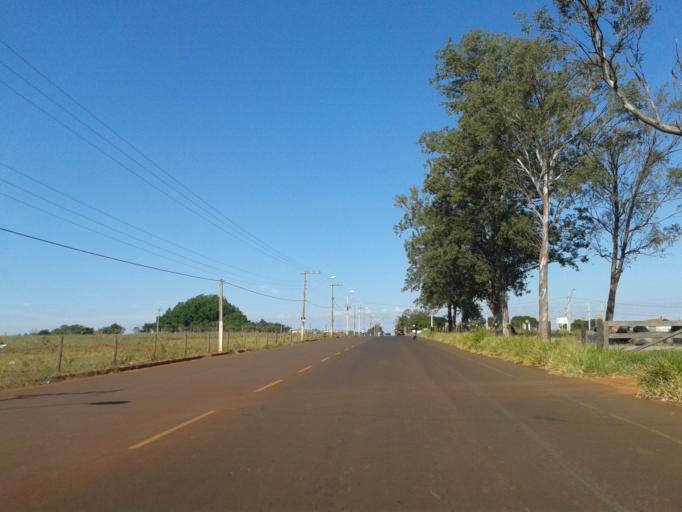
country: BR
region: Minas Gerais
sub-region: Ituiutaba
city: Ituiutaba
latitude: -18.9948
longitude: -49.4881
